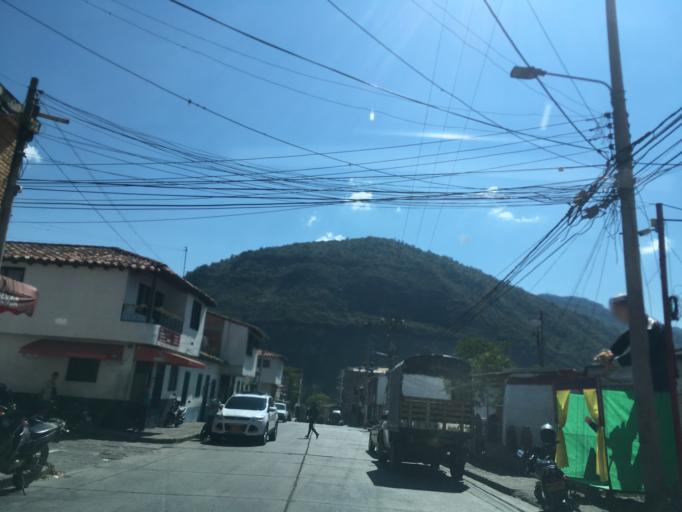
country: CO
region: Santander
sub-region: San Gil
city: San Gil
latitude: 6.5553
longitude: -73.1268
